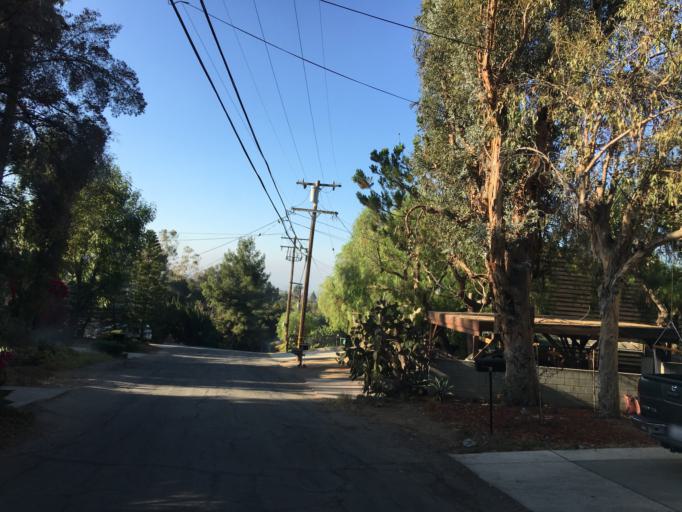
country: US
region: California
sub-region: Los Angeles County
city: San Fernando
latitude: 34.2854
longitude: -118.3739
